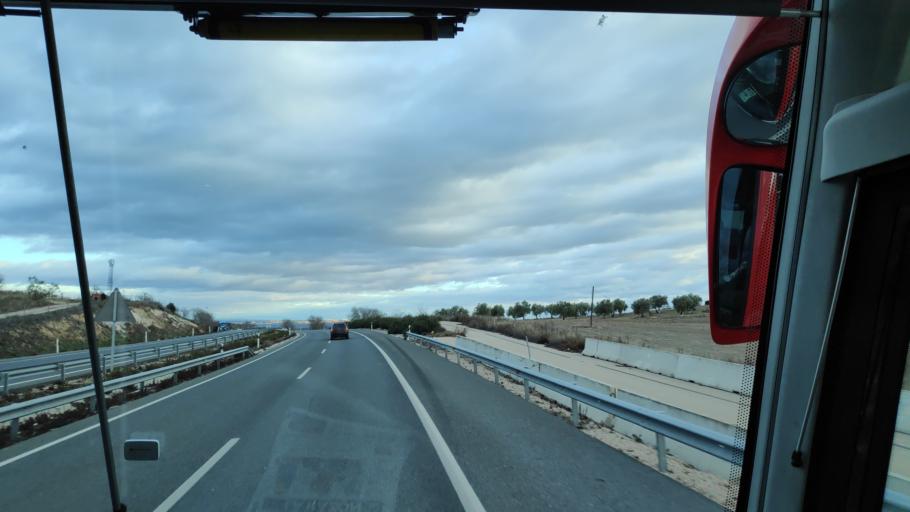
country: ES
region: Madrid
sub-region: Provincia de Madrid
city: Villarejo de Salvanes
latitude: 40.1542
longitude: -3.2511
